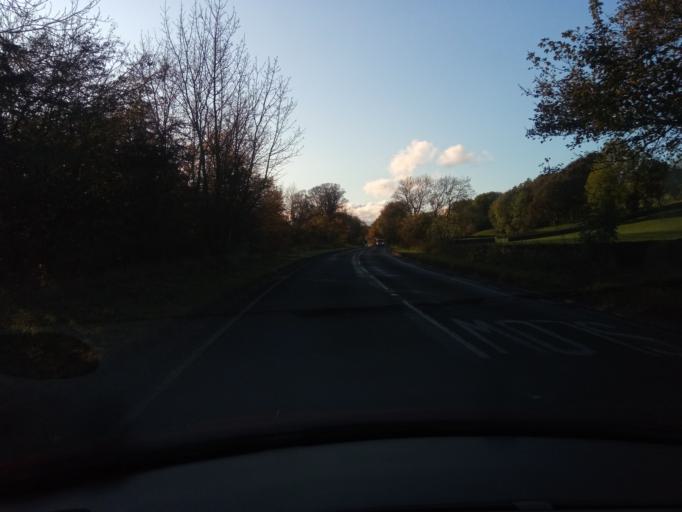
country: GB
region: England
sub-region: County Durham
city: Wolsingham
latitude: 54.7271
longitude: -1.9414
